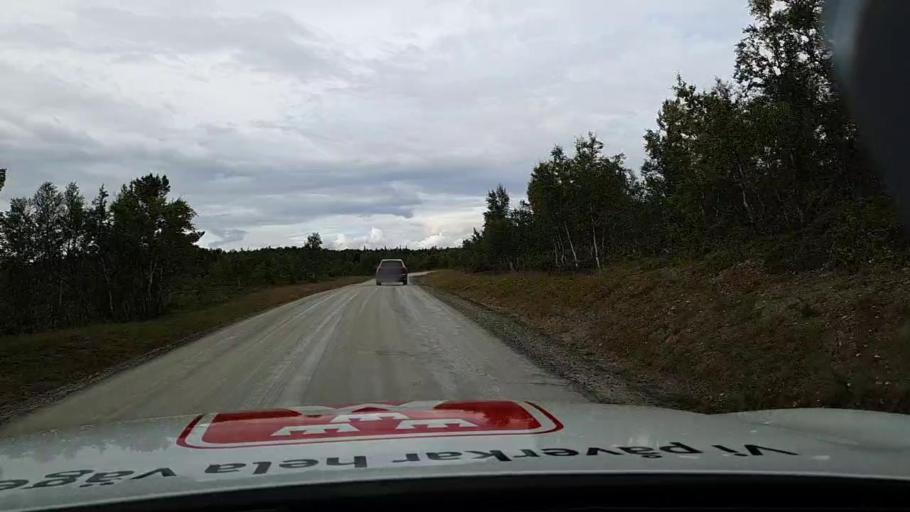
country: SE
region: Jaemtland
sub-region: Are Kommun
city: Are
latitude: 62.6121
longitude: 12.6221
